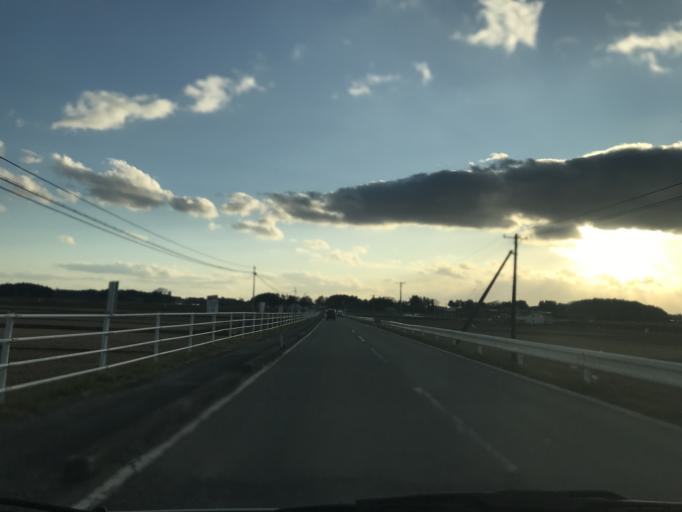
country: JP
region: Miyagi
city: Kogota
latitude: 38.6419
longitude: 141.0727
